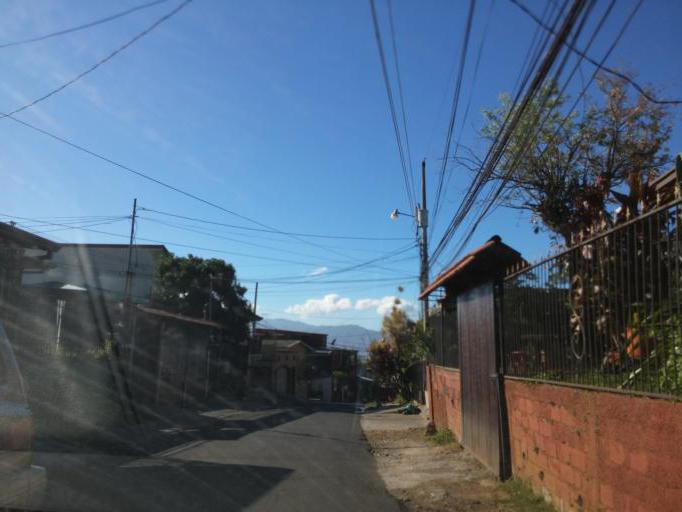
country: CR
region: Alajuela
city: Alajuela
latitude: 10.0332
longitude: -84.2041
